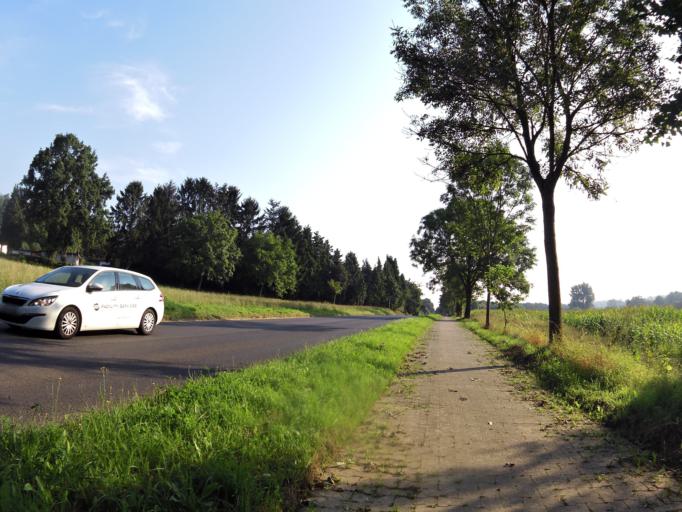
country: DE
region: North Rhine-Westphalia
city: Geilenkirchen
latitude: 50.9552
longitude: 6.1067
